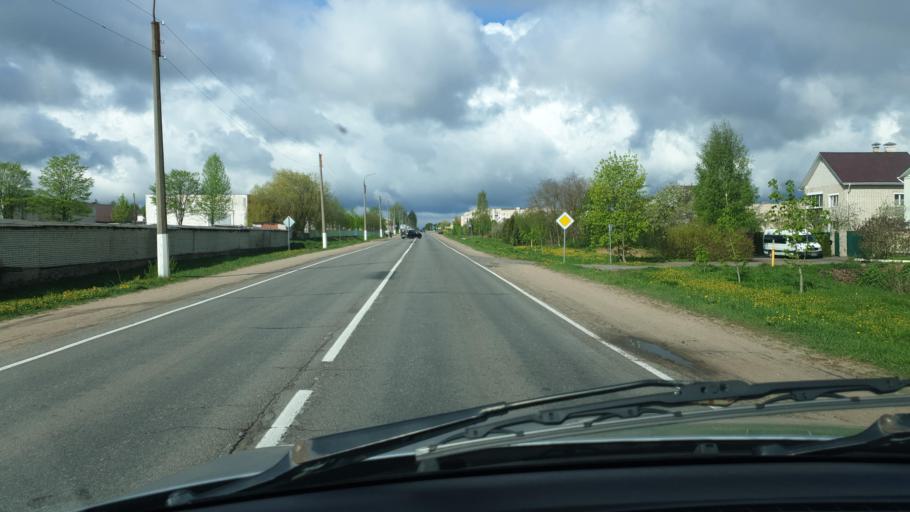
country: BY
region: Vitebsk
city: Lyepyel'
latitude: 54.8811
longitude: 28.7140
